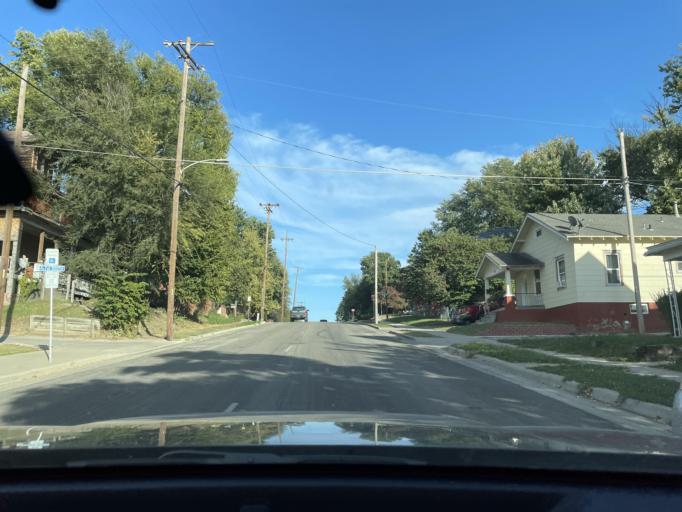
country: US
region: Missouri
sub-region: Buchanan County
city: Saint Joseph
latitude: 39.7683
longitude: -94.8396
